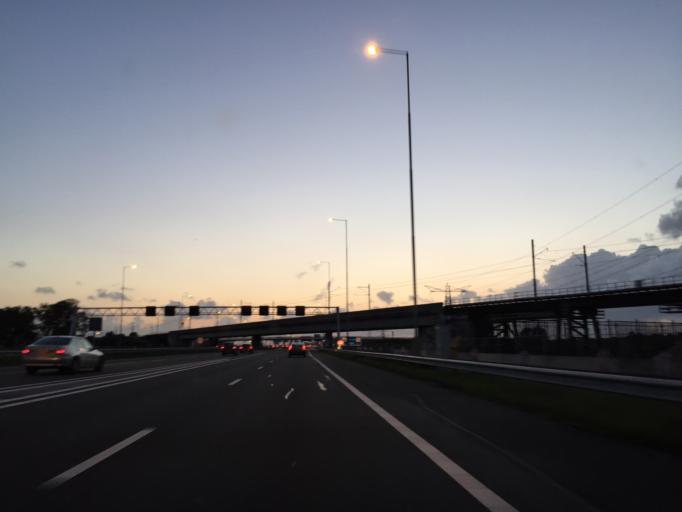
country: NL
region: North Holland
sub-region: Gemeente Weesp
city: Weesp
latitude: 52.3162
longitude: 5.1018
